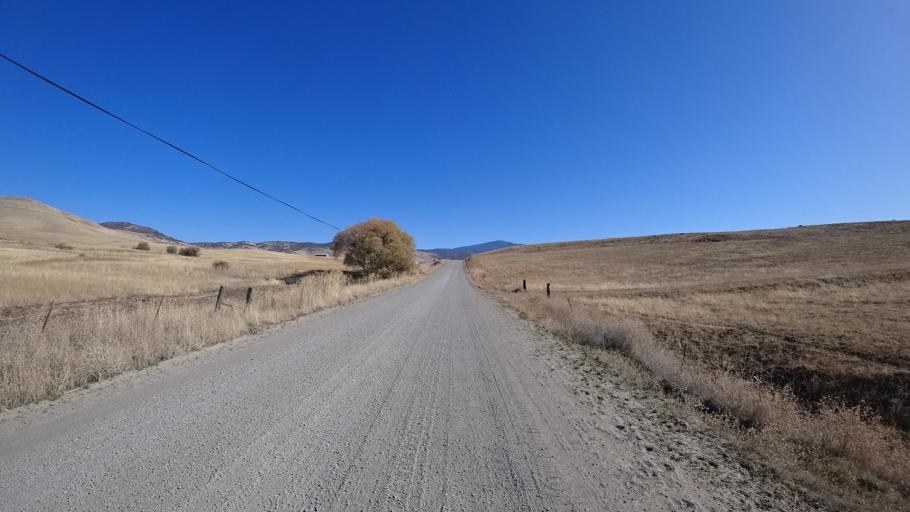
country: US
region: California
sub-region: Siskiyou County
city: Montague
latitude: 41.8298
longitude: -122.4053
